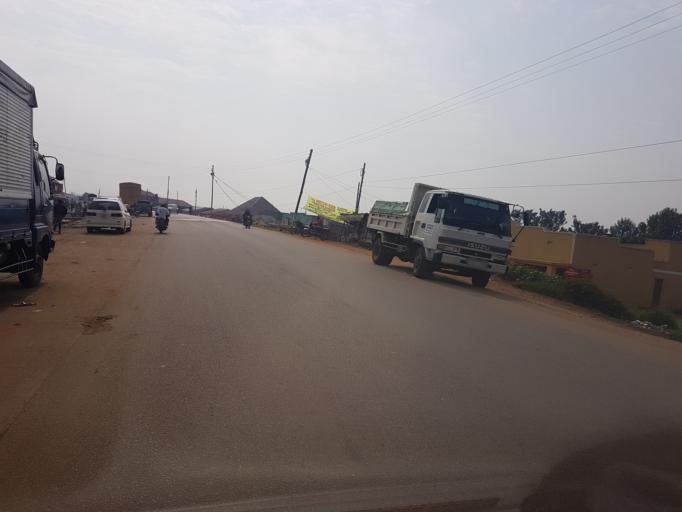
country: UG
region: Western Region
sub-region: Mbarara District
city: Mbarara
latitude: -0.6341
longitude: 30.6196
